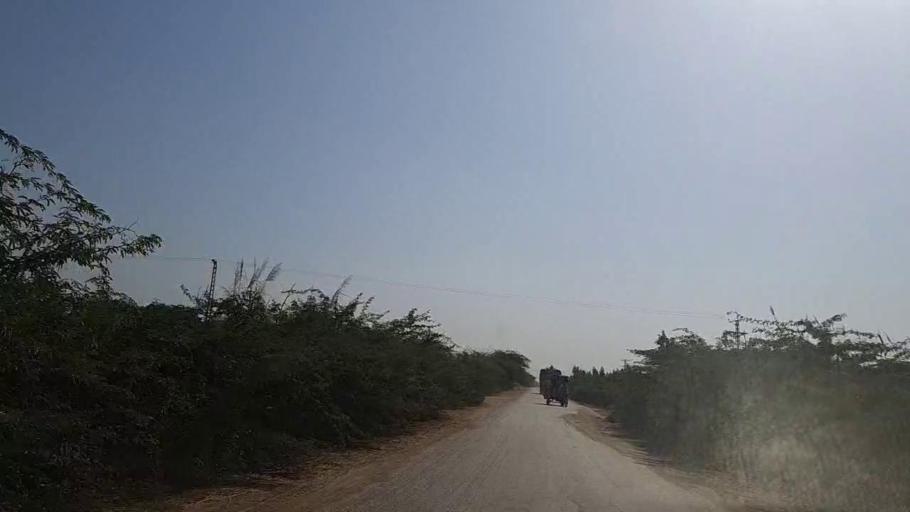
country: PK
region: Sindh
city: Mirpur Batoro
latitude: 24.6033
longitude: 68.2951
